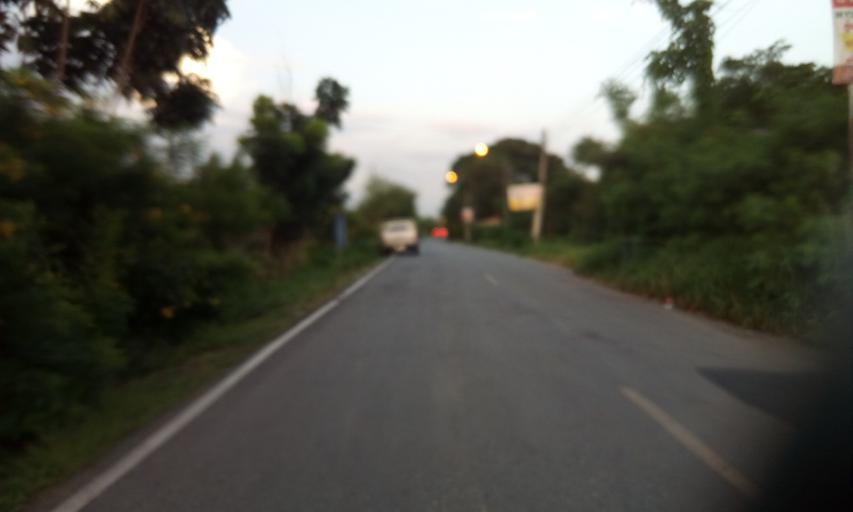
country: TH
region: Pathum Thani
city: Ban Rangsit
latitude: 14.0414
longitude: 100.7934
